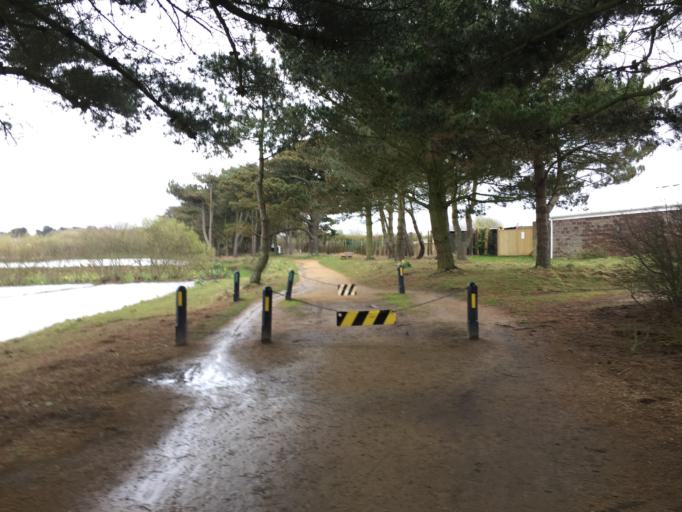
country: JE
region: St Helier
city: Saint Helier
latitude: 49.1810
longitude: -2.2298
